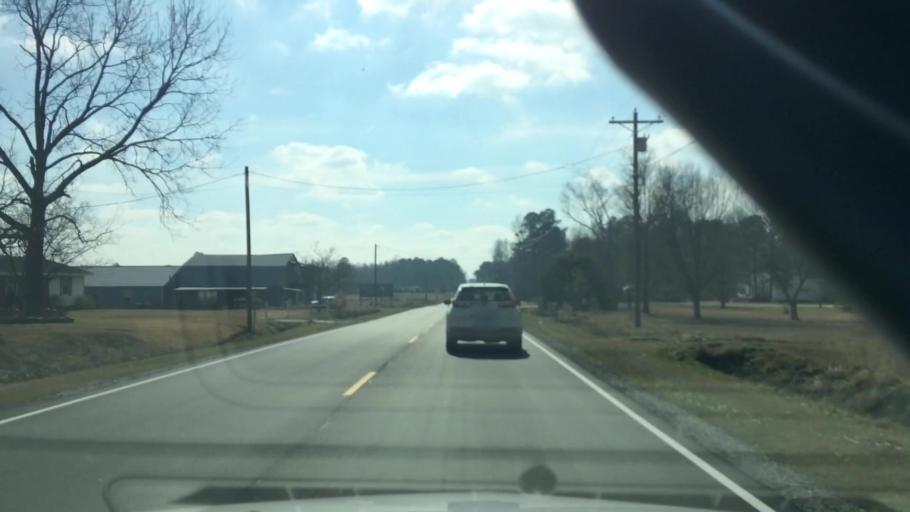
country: US
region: North Carolina
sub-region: Duplin County
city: Beulaville
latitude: 34.9704
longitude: -77.7623
